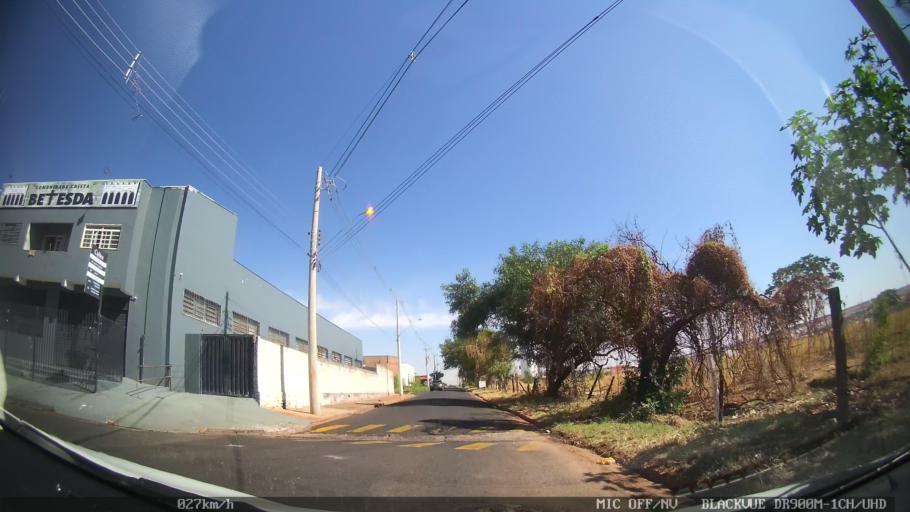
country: BR
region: Sao Paulo
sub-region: Sao Jose Do Rio Preto
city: Sao Jose do Rio Preto
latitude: -20.7661
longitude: -49.4109
